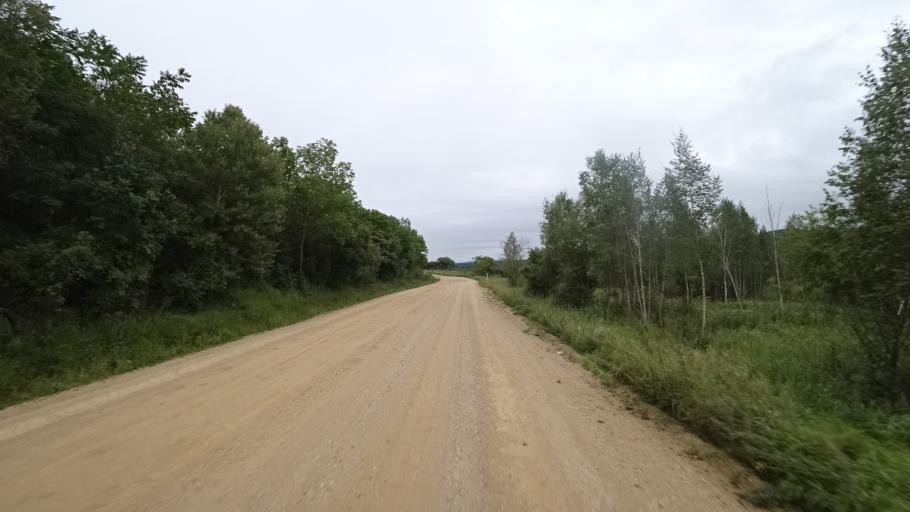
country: RU
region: Primorskiy
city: Rettikhovka
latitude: 44.1770
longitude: 132.8289
